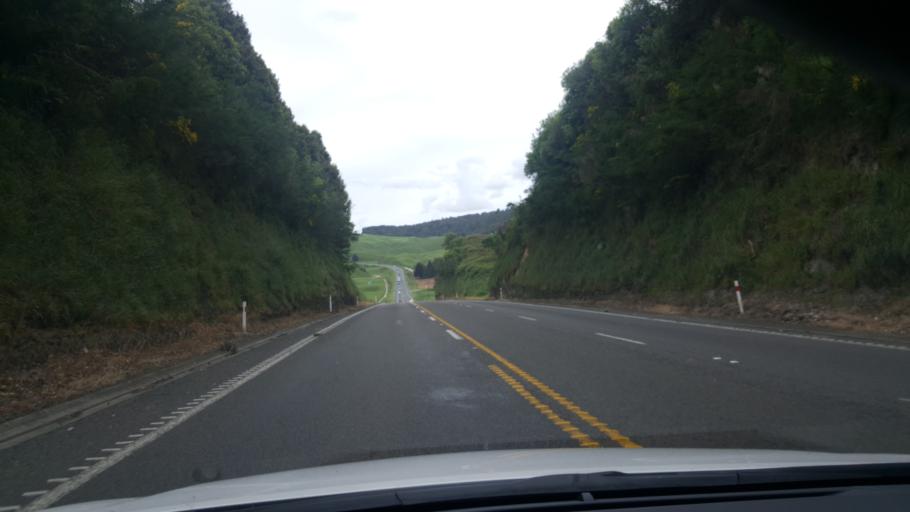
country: NZ
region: Bay of Plenty
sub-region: Rotorua District
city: Rotorua
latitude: -38.2508
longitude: 176.3181
